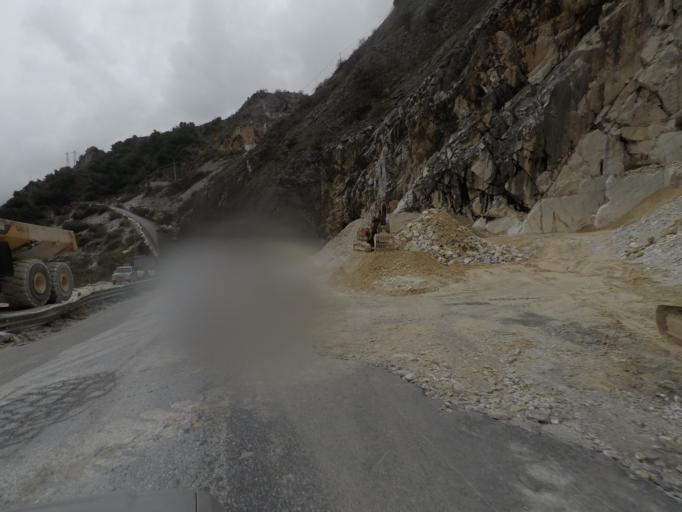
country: IT
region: Tuscany
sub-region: Provincia di Massa-Carrara
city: Massa
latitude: 44.0802
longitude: 10.1338
